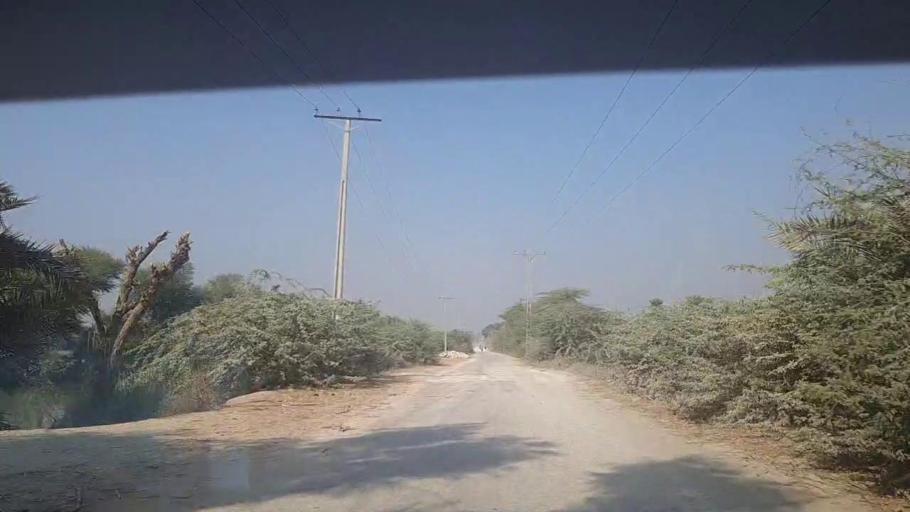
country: PK
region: Sindh
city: Kot Diji
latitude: 27.3554
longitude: 68.7109
